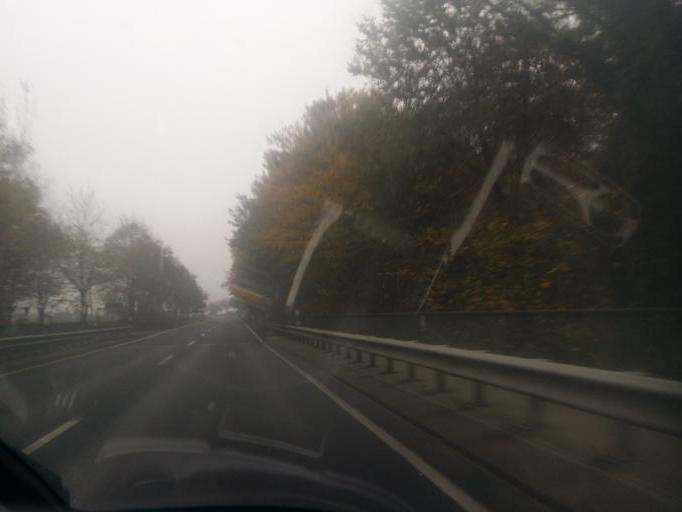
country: DE
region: Schleswig-Holstein
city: Tarp
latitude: 54.6670
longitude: 9.4135
